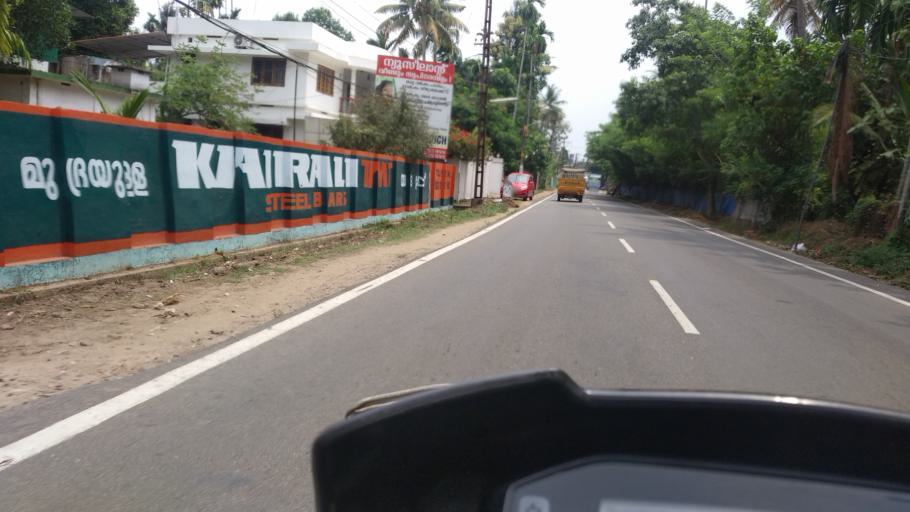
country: IN
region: Kerala
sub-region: Ernakulam
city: Elur
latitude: 10.1007
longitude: 76.2050
